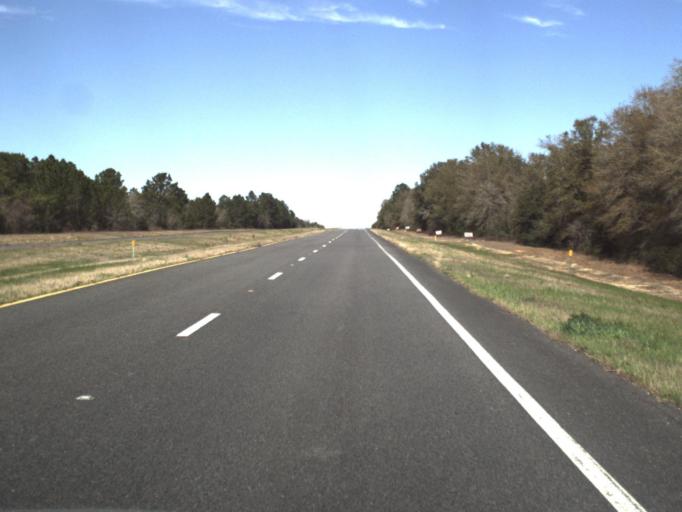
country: US
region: Florida
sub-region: Washington County
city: Chipley
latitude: 30.6151
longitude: -85.3962
